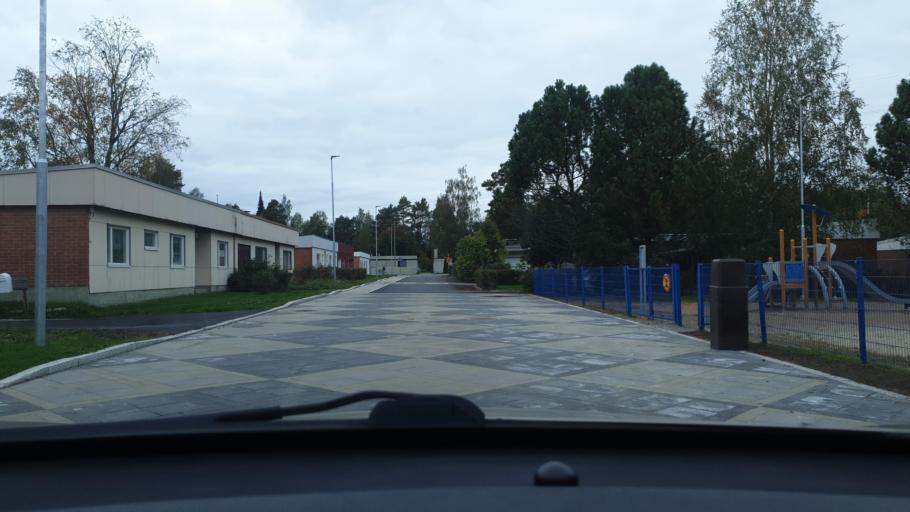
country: FI
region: Ostrobothnia
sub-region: Vaasa
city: Korsholm
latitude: 63.0959
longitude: 21.6710
